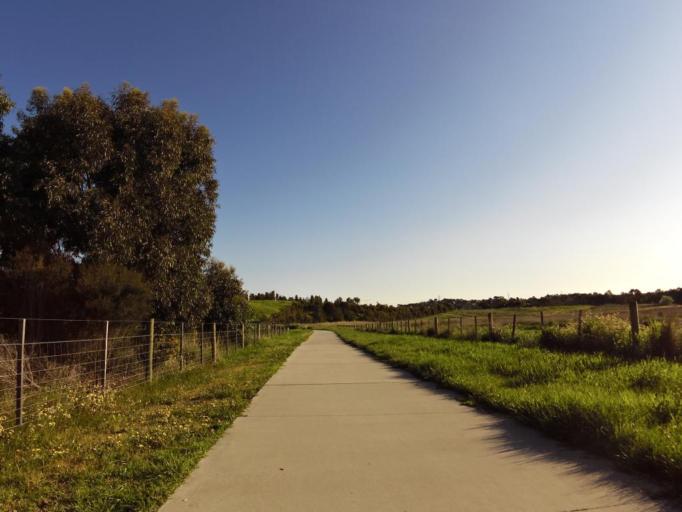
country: AU
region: Victoria
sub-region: Monash
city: Mulgrave
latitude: -37.9225
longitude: 145.2133
